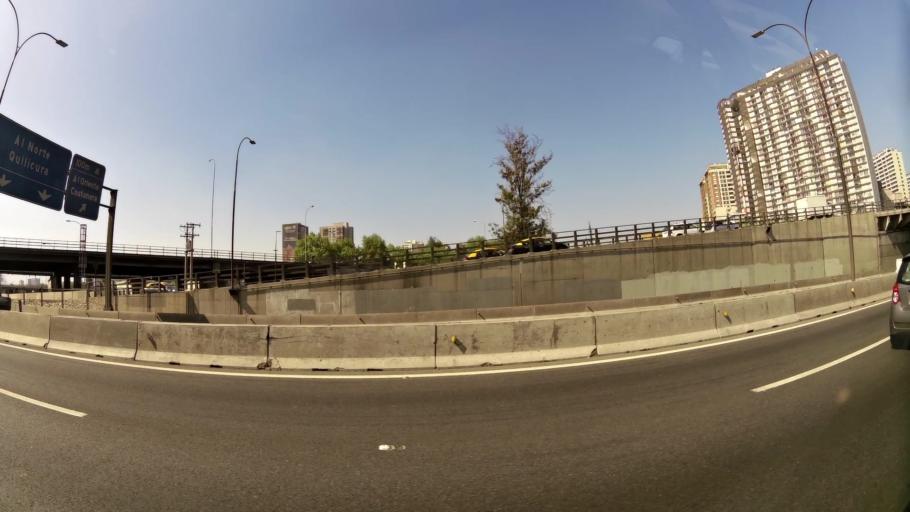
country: CL
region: Santiago Metropolitan
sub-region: Provincia de Santiago
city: Santiago
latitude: -33.4315
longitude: -70.6612
